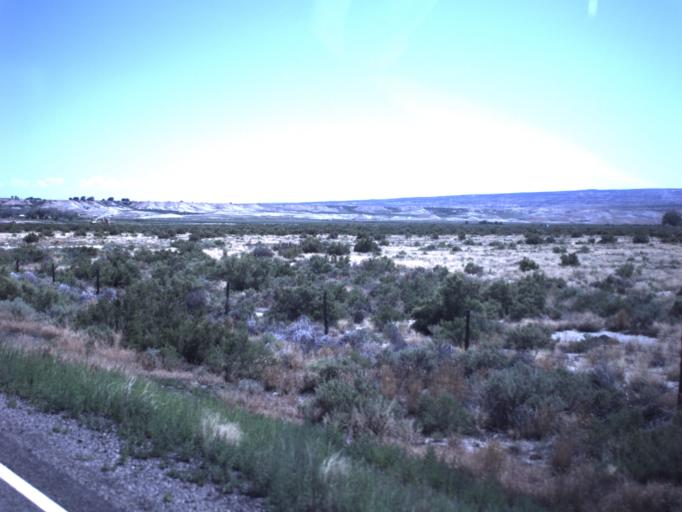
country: US
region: Utah
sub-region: Emery County
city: Ferron
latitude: 38.8599
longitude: -111.3019
